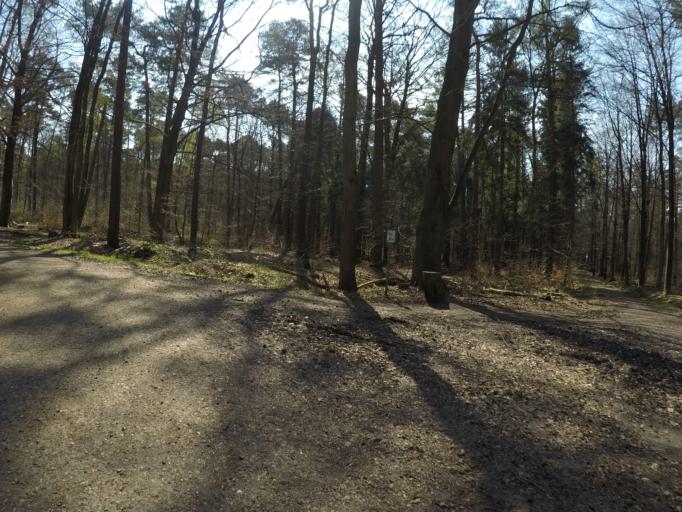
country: DE
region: Schleswig-Holstein
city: Rellingen
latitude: 53.6102
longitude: 9.7857
